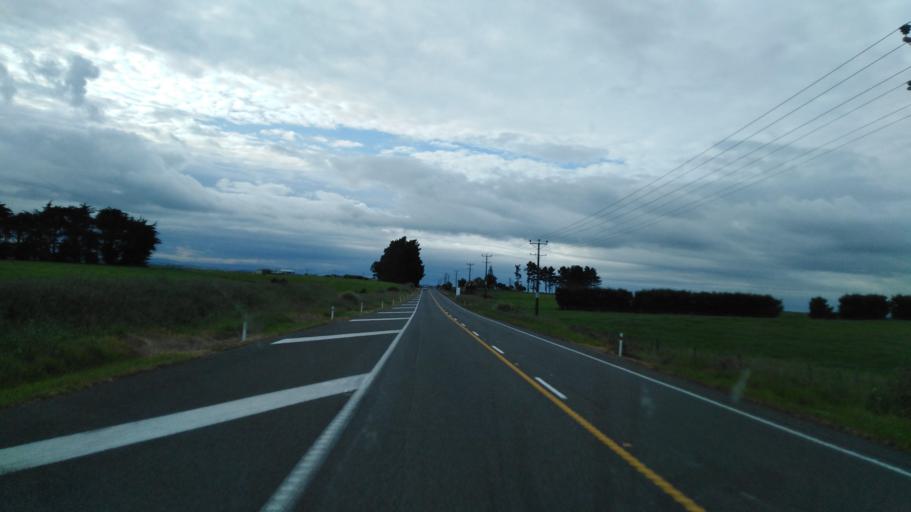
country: NZ
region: Manawatu-Wanganui
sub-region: Rangitikei District
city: Bulls
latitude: -40.1372
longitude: 175.3648
